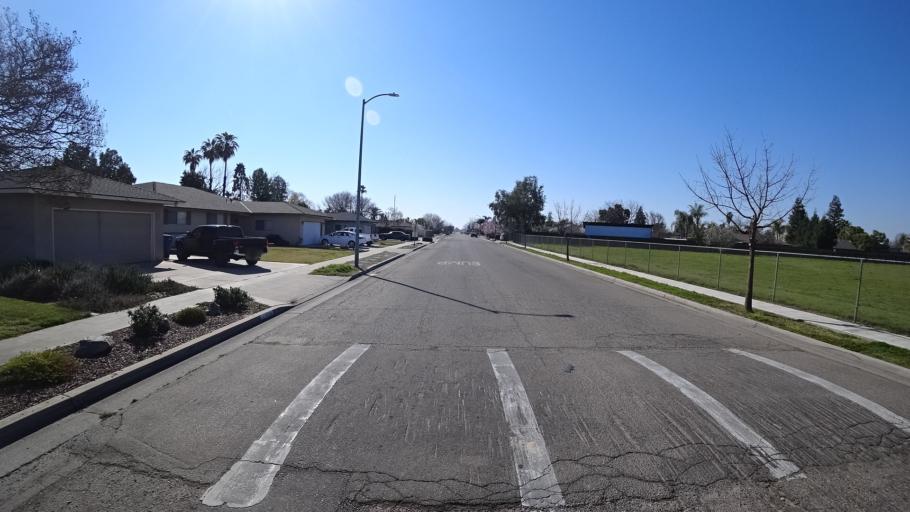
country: US
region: California
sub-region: Fresno County
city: Clovis
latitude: 36.8343
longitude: -119.7452
